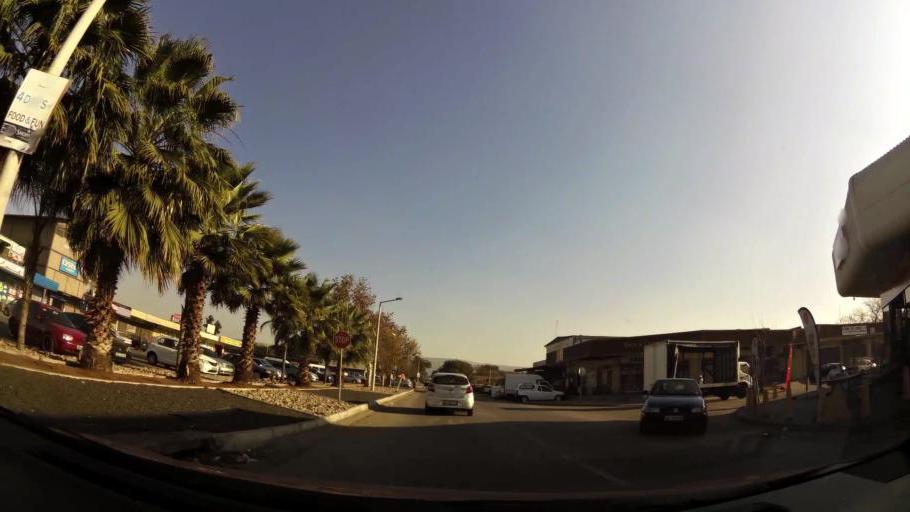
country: ZA
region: North-West
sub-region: Bojanala Platinum District Municipality
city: Rustenburg
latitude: -25.6488
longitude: 27.2395
